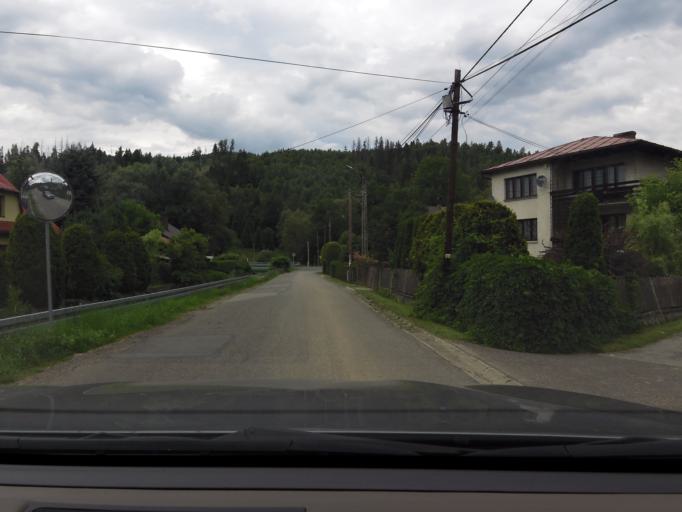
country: PL
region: Silesian Voivodeship
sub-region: Powiat zywiecki
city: Rajcza
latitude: 49.5080
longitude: 19.1120
